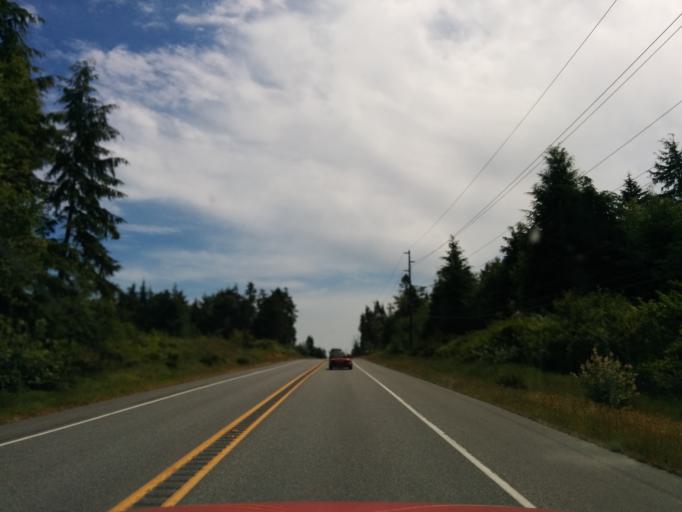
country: US
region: Washington
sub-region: Island County
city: Camano
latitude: 48.1505
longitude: -122.5945
